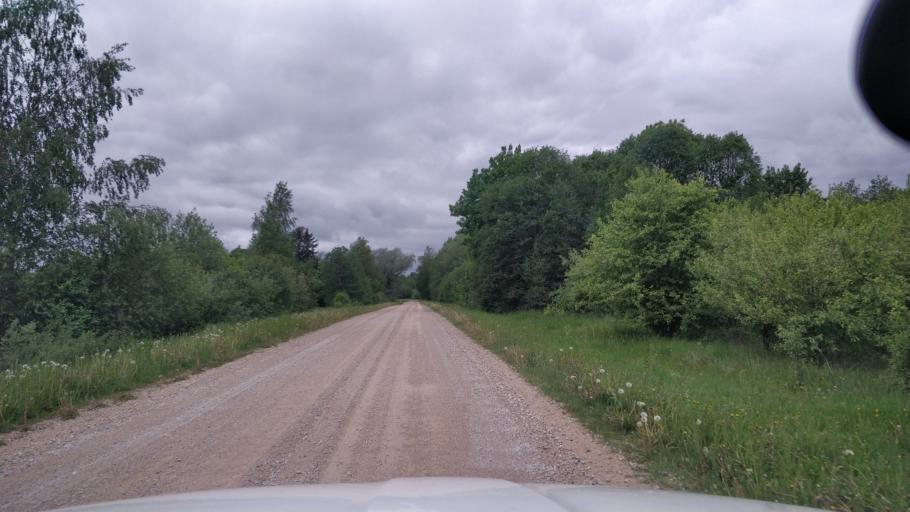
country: EE
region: Paernumaa
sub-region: Halinga vald
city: Parnu-Jaagupi
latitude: 58.7094
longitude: 24.3301
